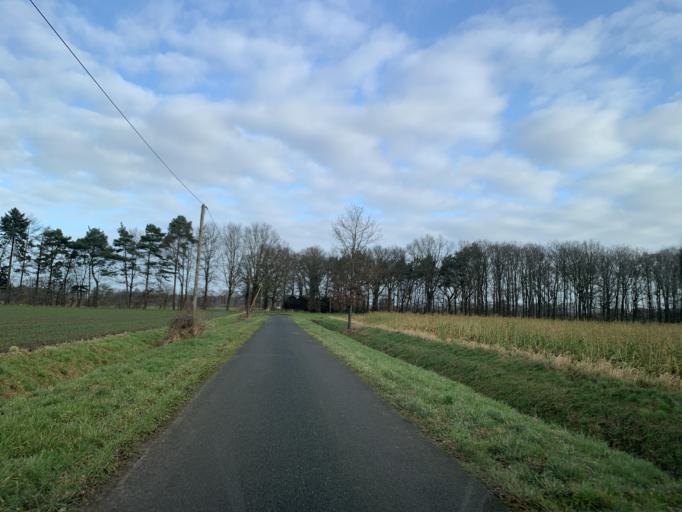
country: DE
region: North Rhine-Westphalia
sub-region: Regierungsbezirk Munster
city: Greven
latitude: 52.0524
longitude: 7.6239
